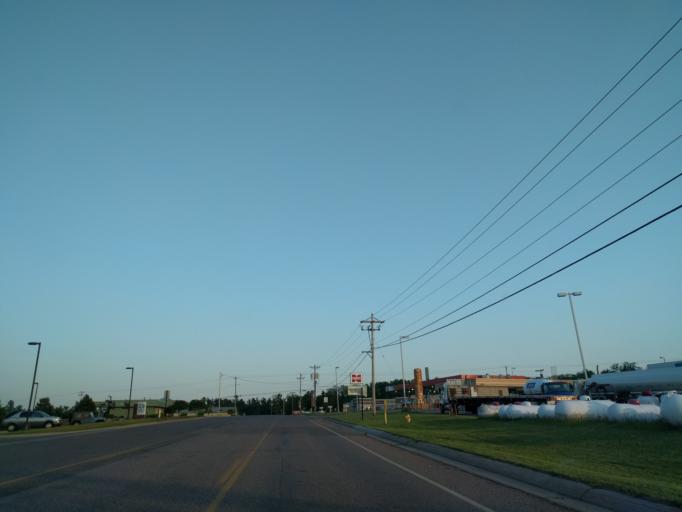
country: US
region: Michigan
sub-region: Marquette County
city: Trowbridge Park
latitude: 46.5511
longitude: -87.4569
